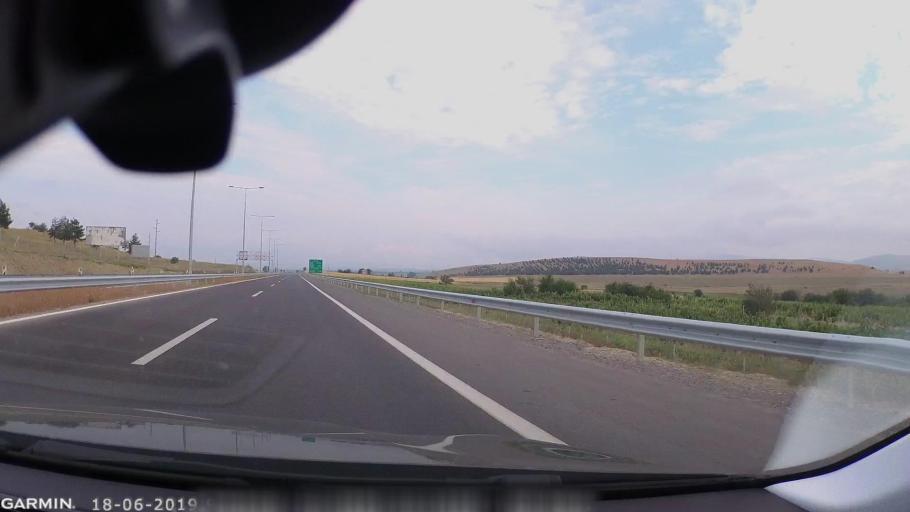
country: MK
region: Stip
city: Shtip
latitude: 41.7838
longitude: 22.1223
